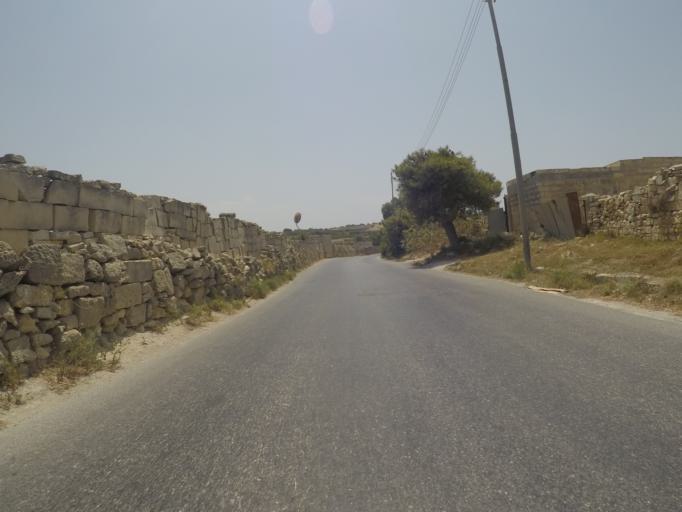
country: MT
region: Is-Siggiewi
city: Siggiewi
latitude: 35.8590
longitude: 14.4202
